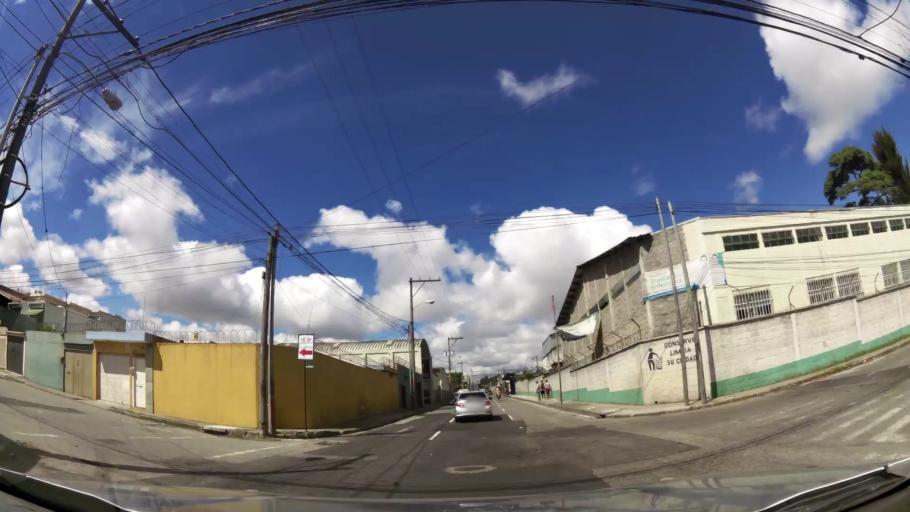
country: GT
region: Guatemala
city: Guatemala City
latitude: 14.6028
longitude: -90.5302
